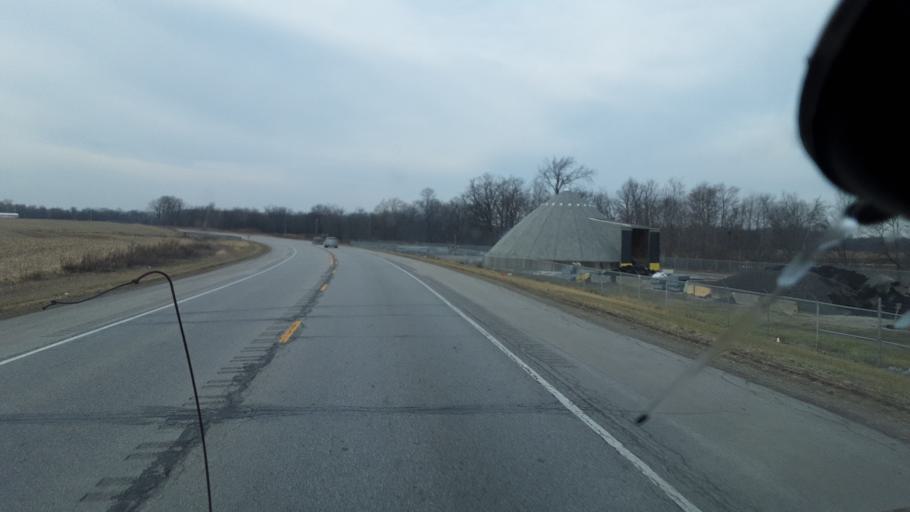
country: US
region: Indiana
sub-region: DeKalb County
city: Waterloo
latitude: 41.4379
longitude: -85.0362
